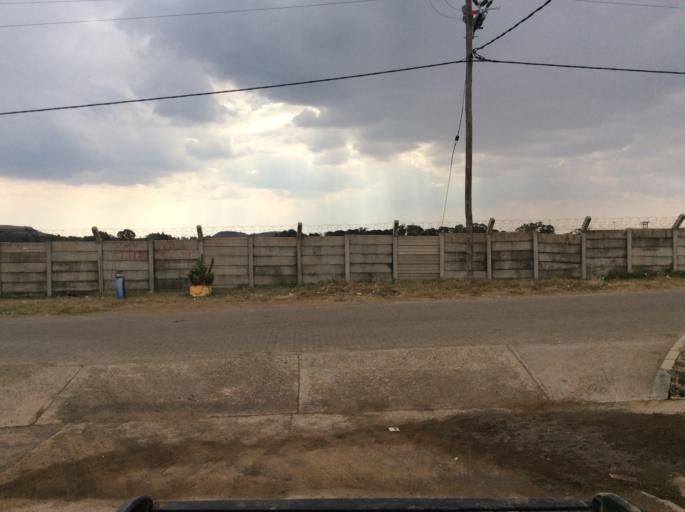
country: ZA
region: Orange Free State
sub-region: Xhariep District Municipality
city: Dewetsdorp
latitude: -29.5825
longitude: 26.6783
